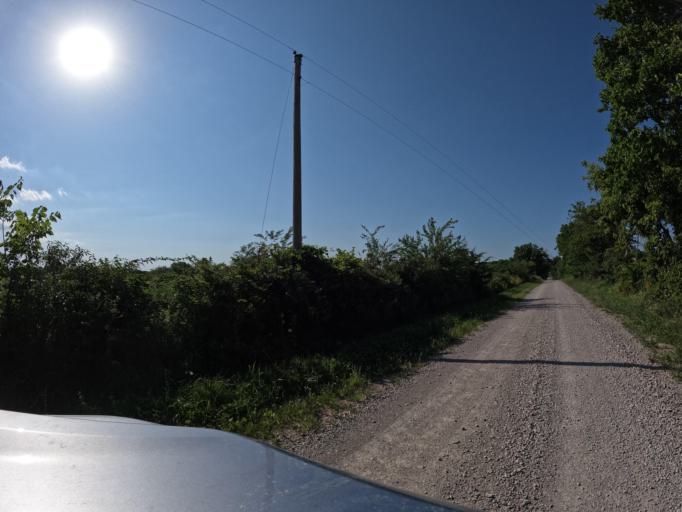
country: US
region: Iowa
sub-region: Appanoose County
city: Centerville
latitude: 40.7273
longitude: -93.0159
